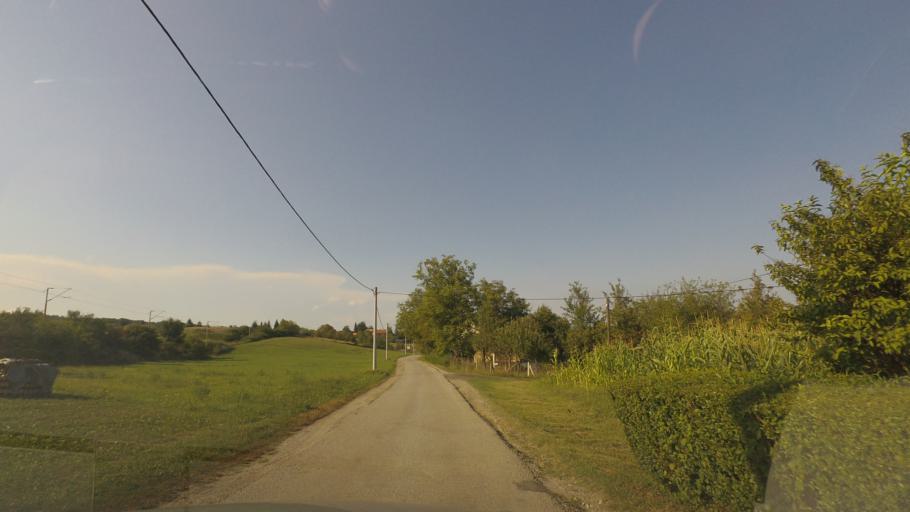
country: HR
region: Karlovacka
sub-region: Grad Karlovac
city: Karlovac
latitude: 45.4168
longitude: 15.4752
